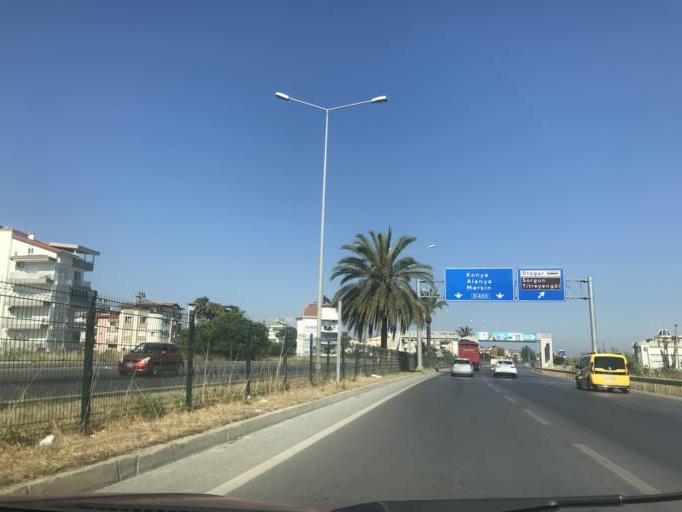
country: TR
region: Antalya
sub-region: Manavgat
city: Manavgat
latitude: 36.7831
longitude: 31.4214
